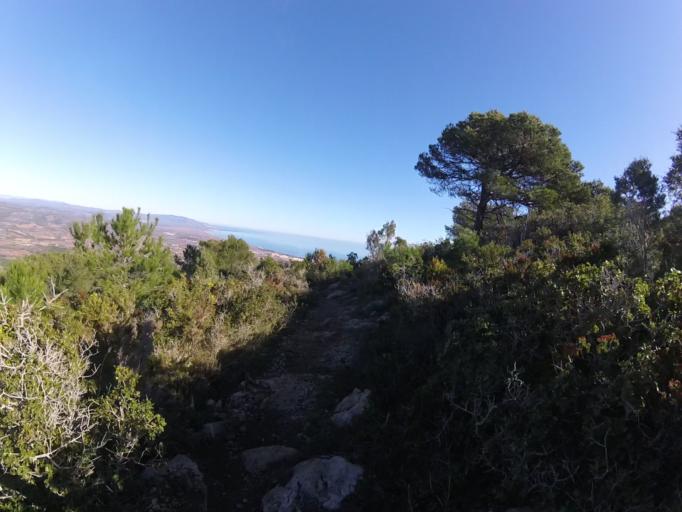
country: ES
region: Valencia
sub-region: Provincia de Castello
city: Orpesa/Oropesa del Mar
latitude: 40.1011
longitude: 0.1123
